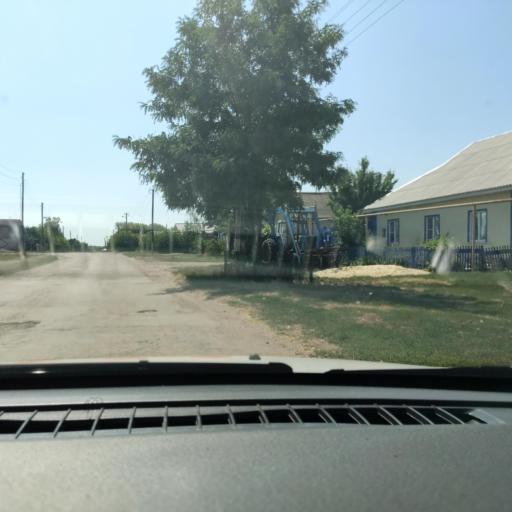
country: RU
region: Voronezj
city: Ol'khovatka
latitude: 50.5700
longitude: 39.2620
